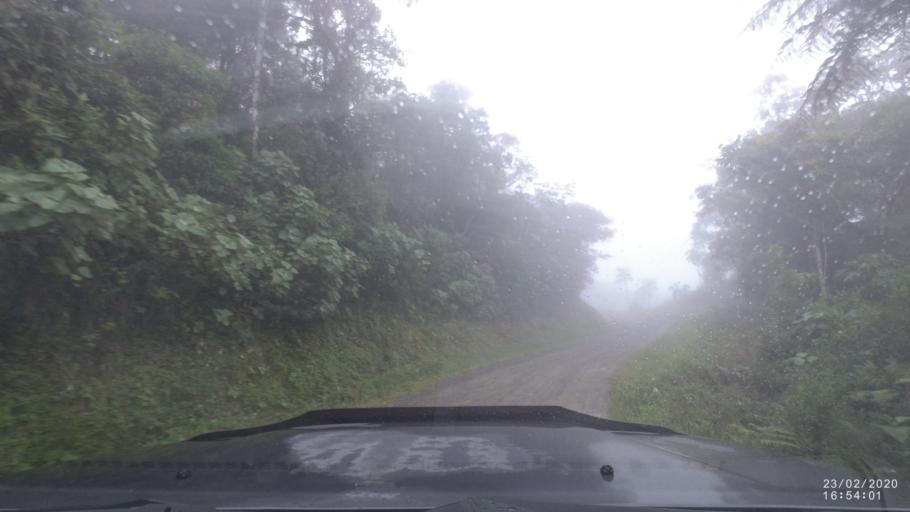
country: BO
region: Cochabamba
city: Colomi
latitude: -17.0987
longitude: -65.9828
